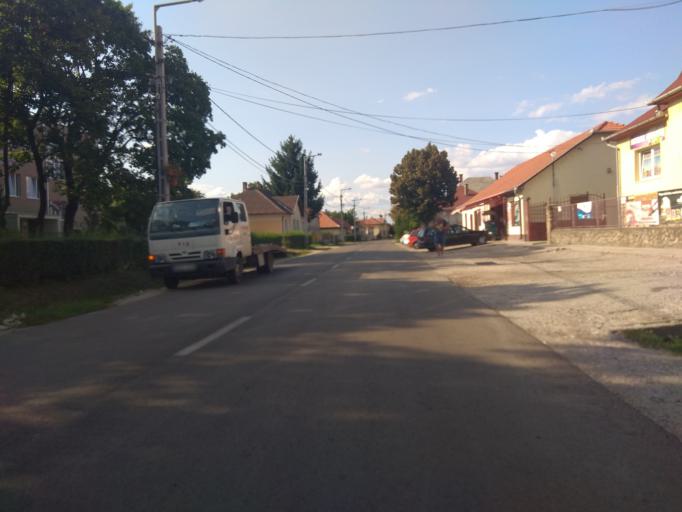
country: HU
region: Borsod-Abauj-Zemplen
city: Mezocsat
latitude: 47.8239
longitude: 20.9026
